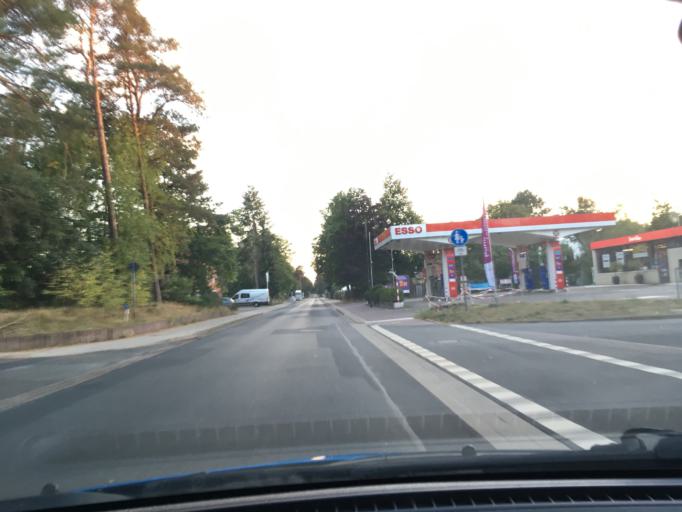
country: DE
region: Lower Saxony
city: Fassberg
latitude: 52.8986
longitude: 10.1676
